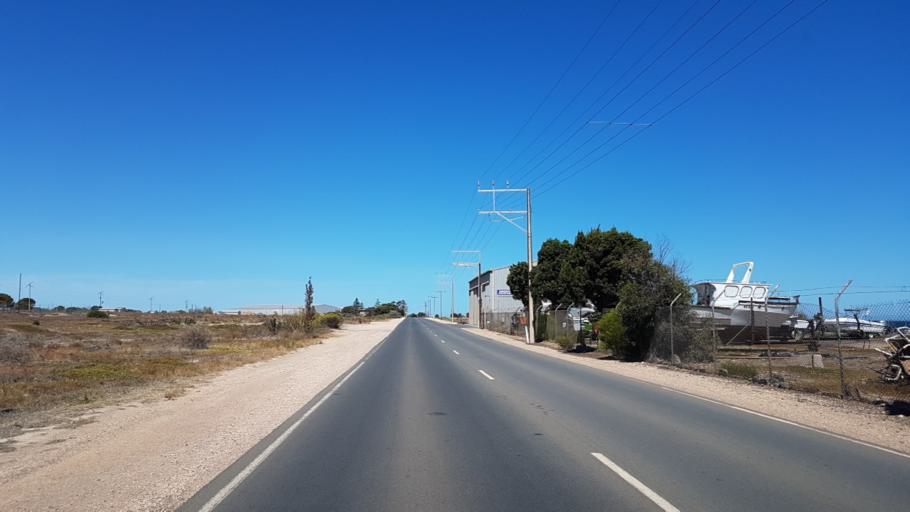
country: AU
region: South Australia
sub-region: Copper Coast
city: Wallaroo
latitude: -33.9325
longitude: 137.6121
